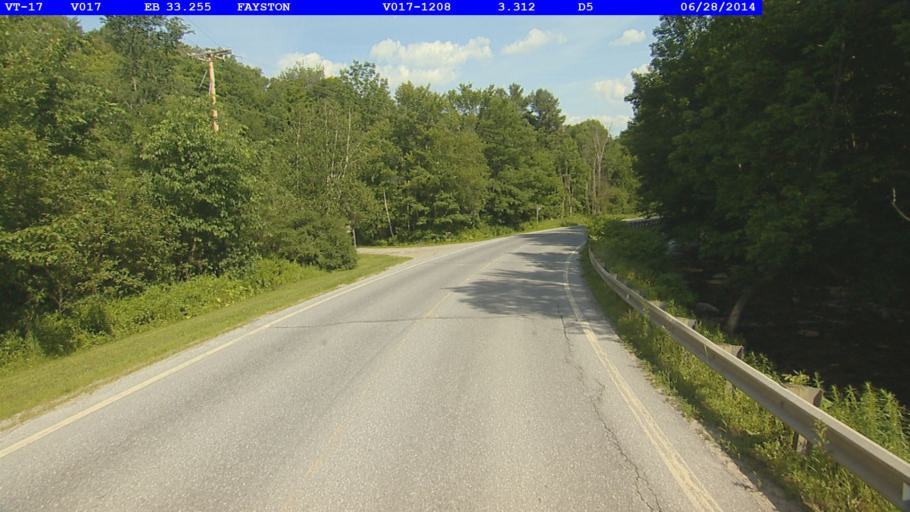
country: US
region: Vermont
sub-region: Washington County
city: Waterbury
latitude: 44.1926
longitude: -72.8863
